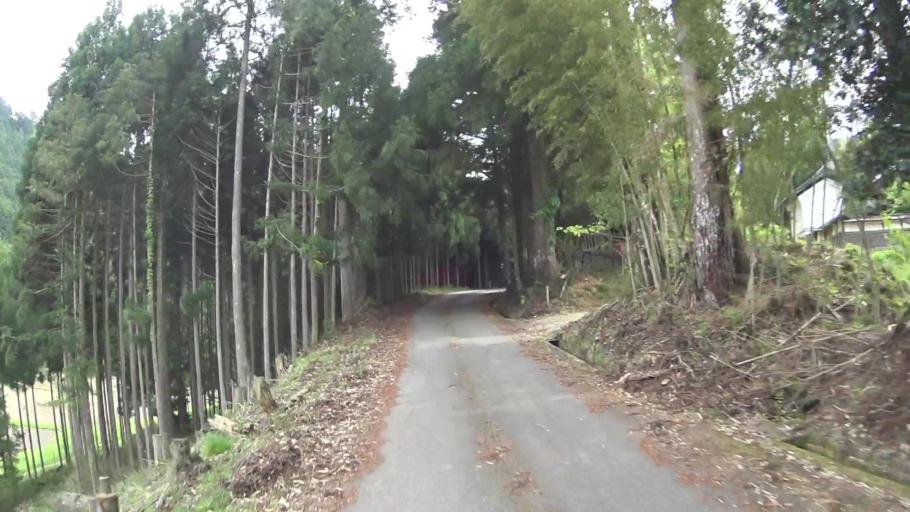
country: JP
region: Kyoto
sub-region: Kyoto-shi
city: Kamigyo-ku
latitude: 35.1970
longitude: 135.7025
